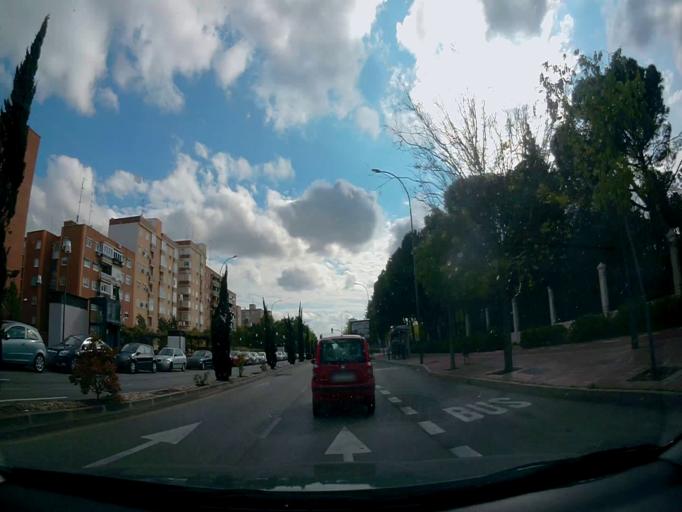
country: ES
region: Madrid
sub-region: Provincia de Madrid
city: Mostoles
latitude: 40.3238
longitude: -3.8718
